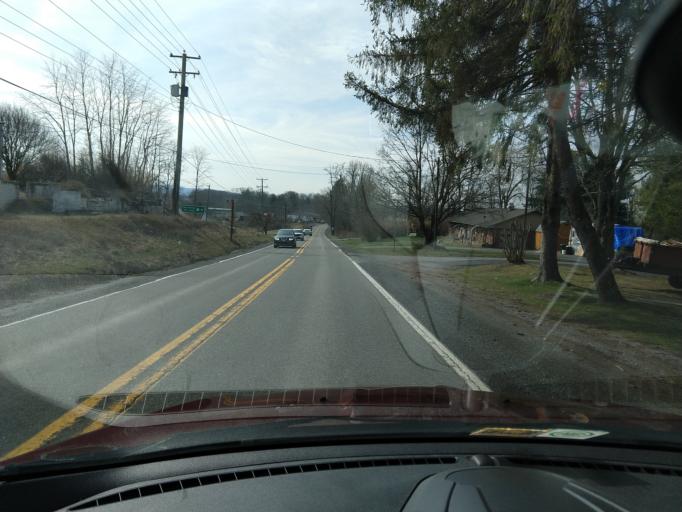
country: US
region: West Virginia
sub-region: Greenbrier County
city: Lewisburg
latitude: 37.8640
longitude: -80.4101
